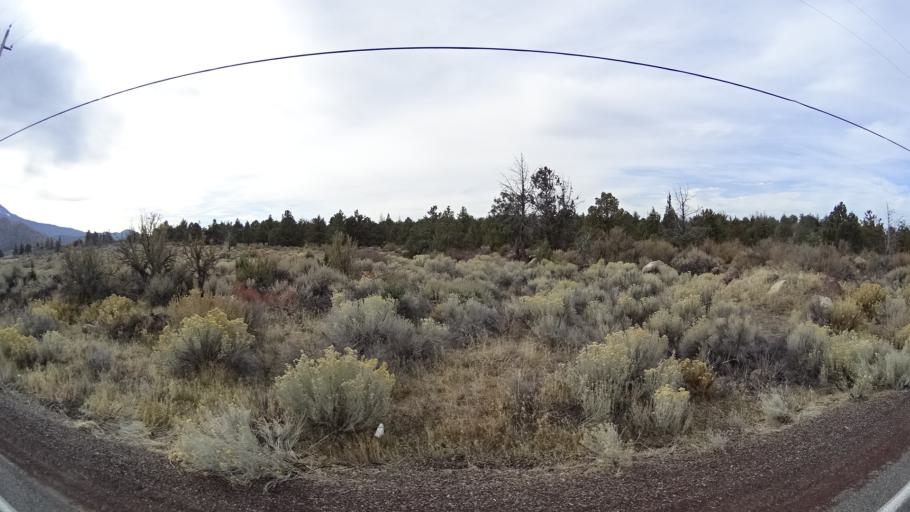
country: US
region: California
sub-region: Siskiyou County
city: Weed
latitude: 41.5672
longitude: -122.2660
